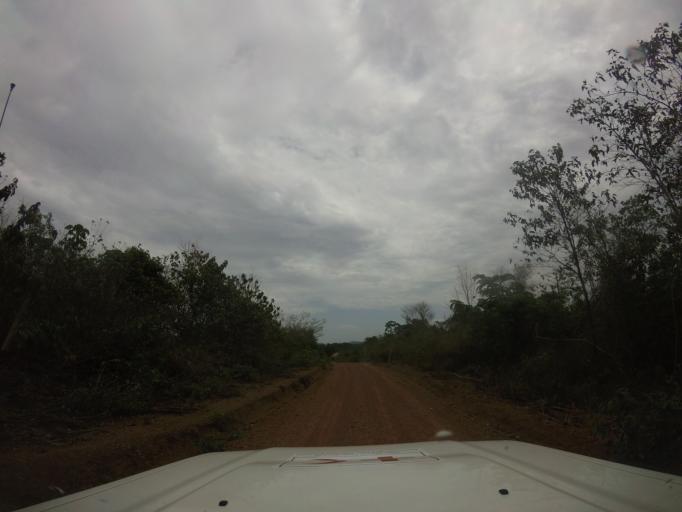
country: SL
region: Southern Province
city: Zimmi
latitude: 7.2273
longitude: -11.1933
